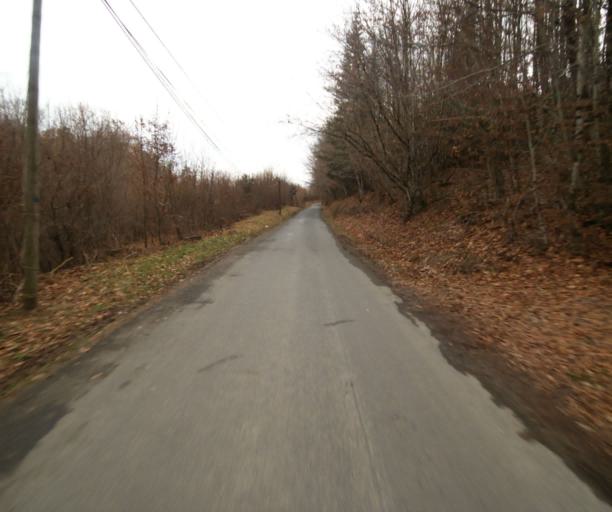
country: FR
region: Limousin
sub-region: Departement de la Correze
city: Chameyrat
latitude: 45.2364
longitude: 1.6879
